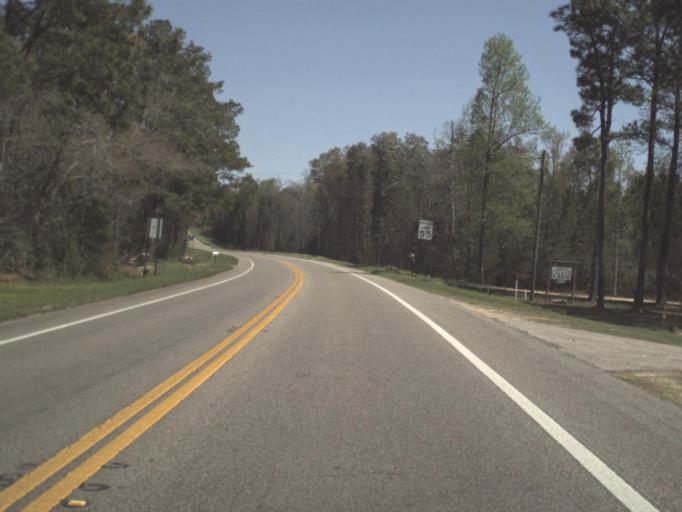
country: US
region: Florida
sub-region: Calhoun County
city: Blountstown
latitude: 30.4263
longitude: -85.1635
